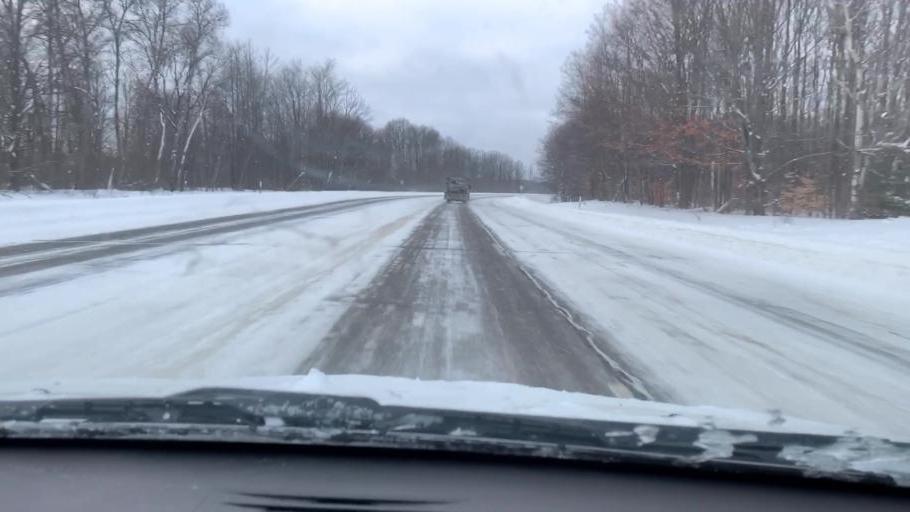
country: US
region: Michigan
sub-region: Kalkaska County
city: Kalkaska
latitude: 44.6166
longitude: -85.3037
